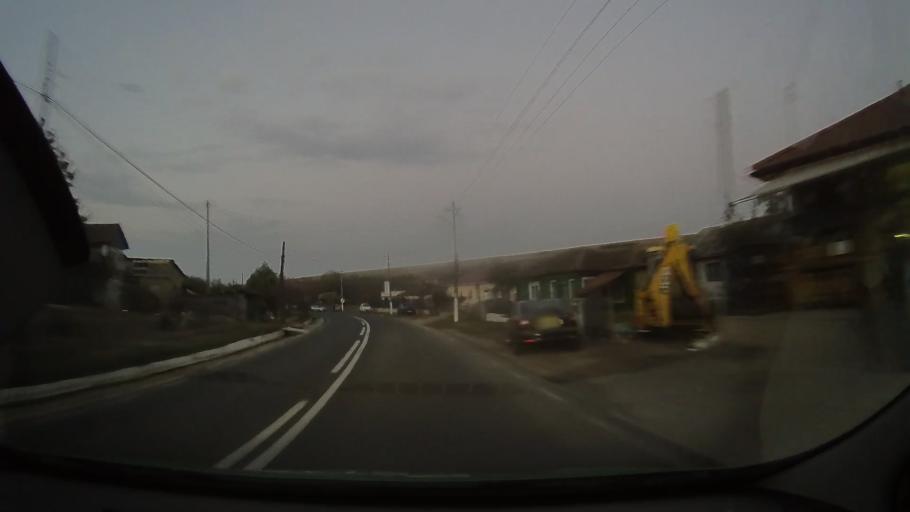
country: RO
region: Constanta
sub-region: Comuna Ion Corvin
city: Ion Corvin
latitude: 44.0956
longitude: 27.7540
